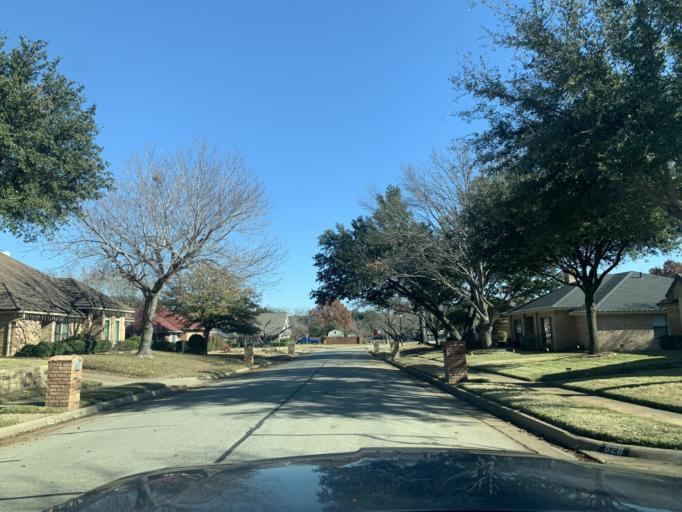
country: US
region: Texas
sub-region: Tarrant County
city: Bedford
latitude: 32.8442
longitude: -97.1546
